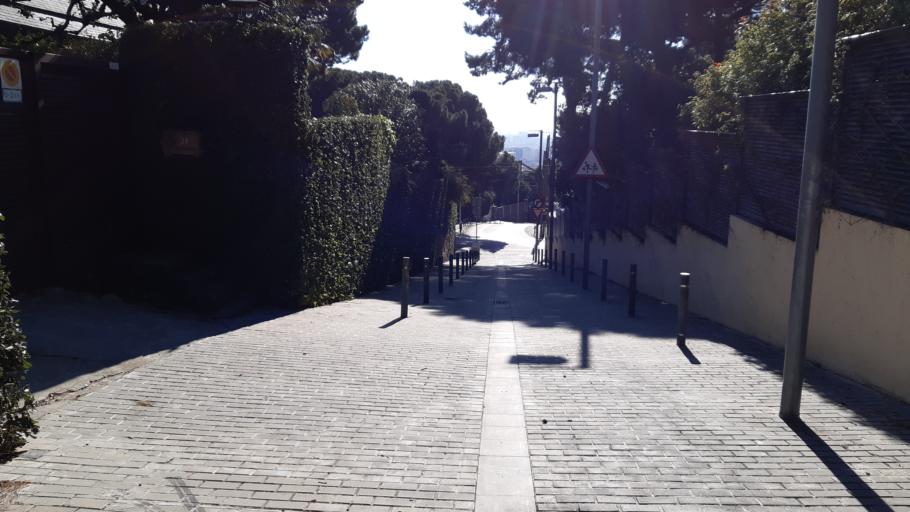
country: ES
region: Catalonia
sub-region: Provincia de Barcelona
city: Esplugues de Llobregat
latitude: 41.3920
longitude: 2.1060
